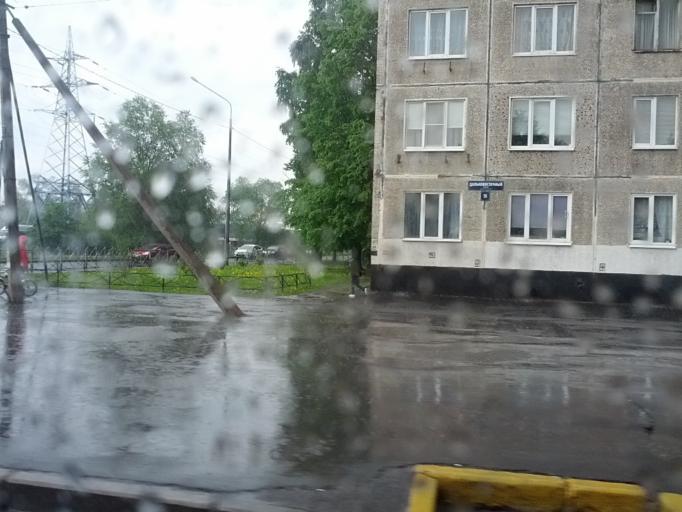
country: RU
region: St.-Petersburg
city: Obukhovo
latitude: 59.8843
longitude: 30.4678
